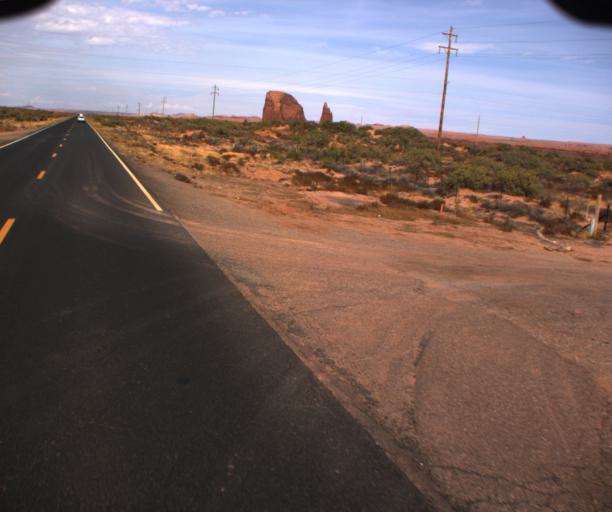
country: US
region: Arizona
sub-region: Apache County
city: Many Farms
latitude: 36.6400
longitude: -109.5883
